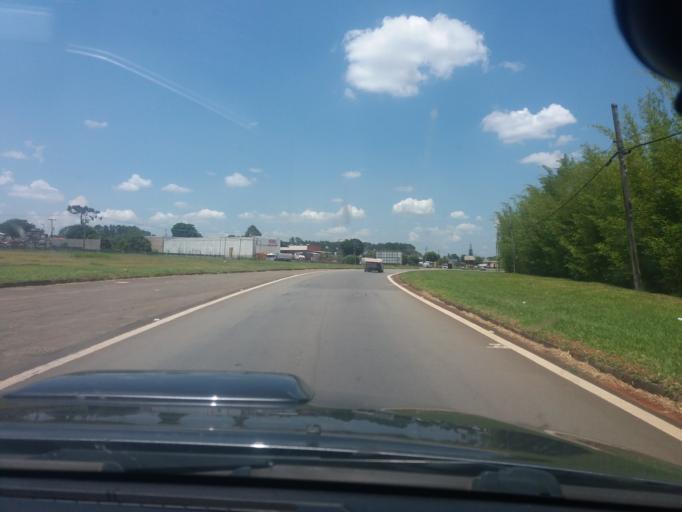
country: BR
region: Sao Paulo
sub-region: Itapetininga
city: Itapetininga
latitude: -23.5919
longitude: -47.9877
